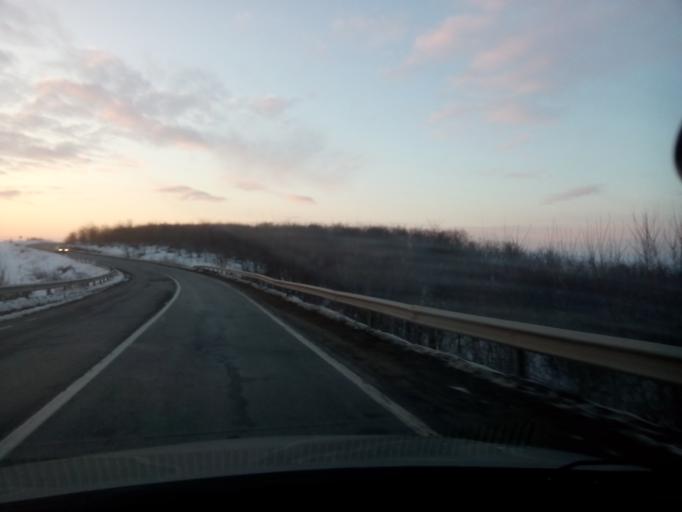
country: RO
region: Giurgiu
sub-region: Comuna Herasti
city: Herasti
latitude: 44.2410
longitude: 26.3975
